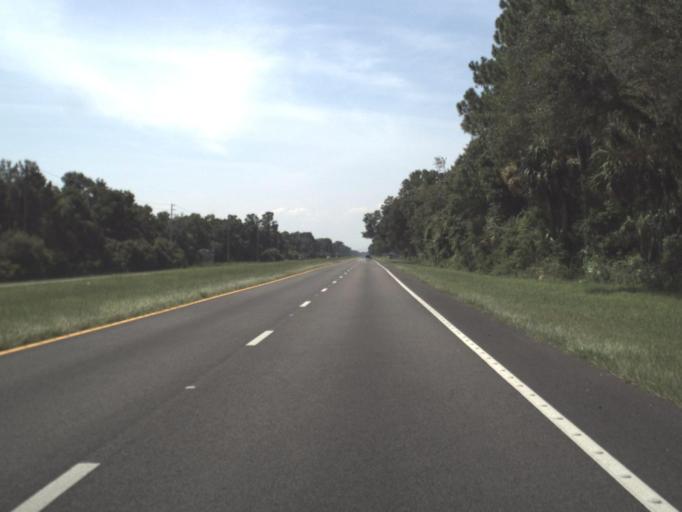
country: US
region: Florida
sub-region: Citrus County
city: Crystal River
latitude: 28.9352
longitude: -82.6180
